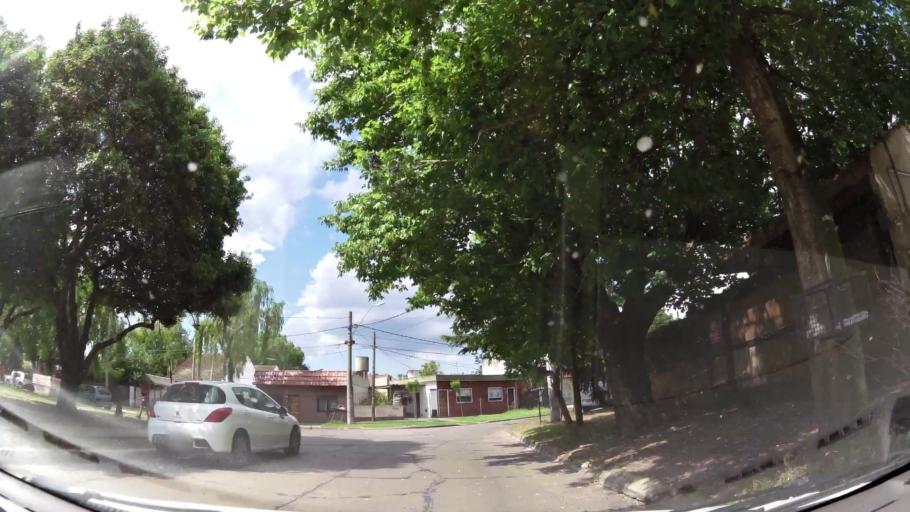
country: AR
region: Buenos Aires
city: Ituzaingo
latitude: -34.6410
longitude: -58.6699
